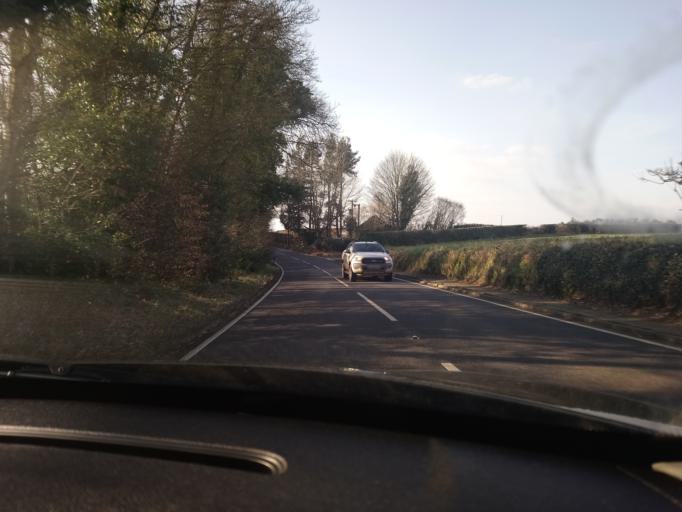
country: GB
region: England
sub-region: Shropshire
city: Clive
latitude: 52.7998
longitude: -2.7614
